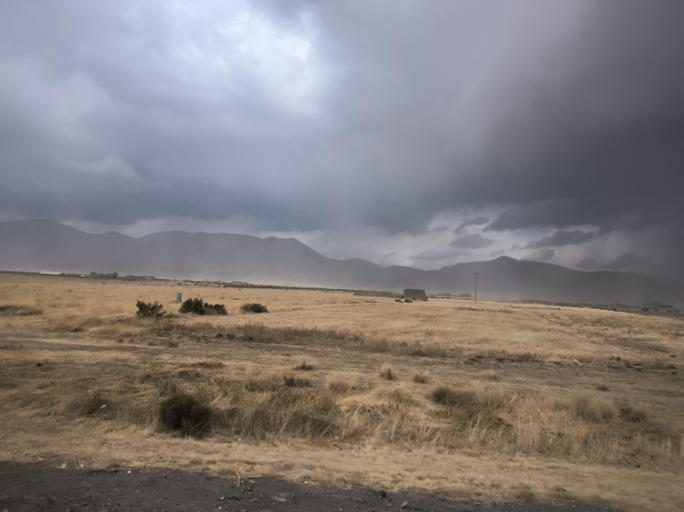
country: BO
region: Oruro
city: Challapata
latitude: -18.7770
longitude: -66.8527
